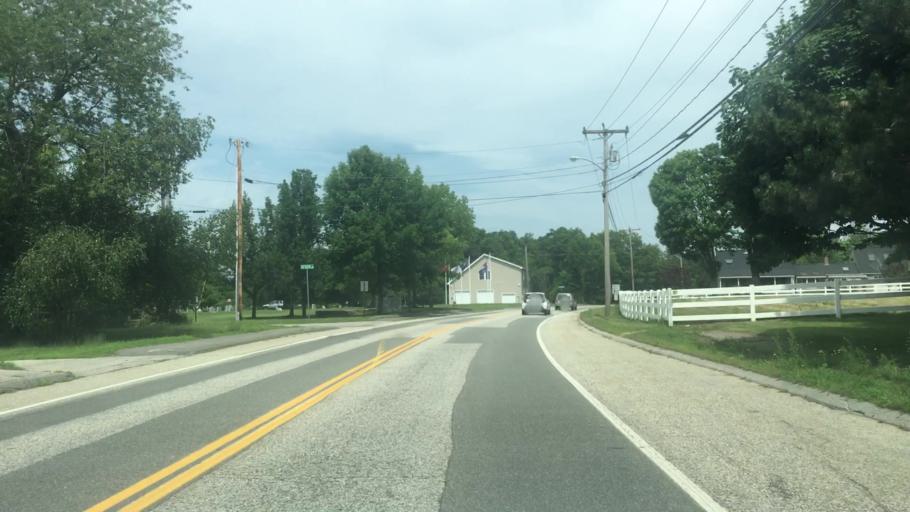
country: US
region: Maine
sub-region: Cumberland County
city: South Portland Gardens
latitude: 43.6148
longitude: -70.2779
